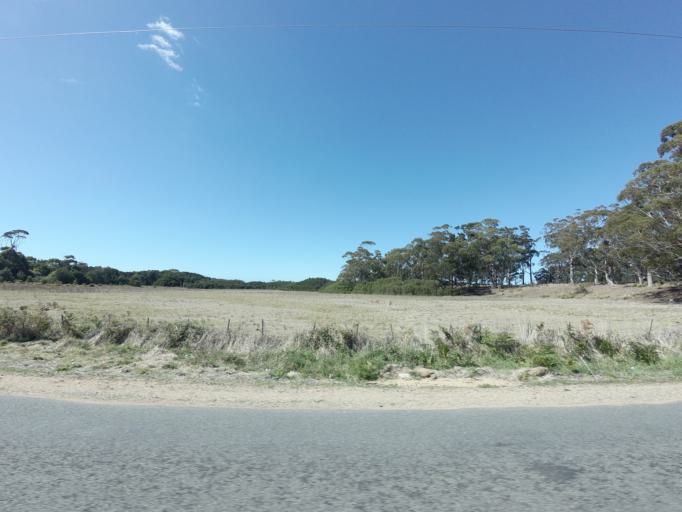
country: AU
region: Tasmania
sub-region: Break O'Day
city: St Helens
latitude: -41.6856
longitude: 148.2814
